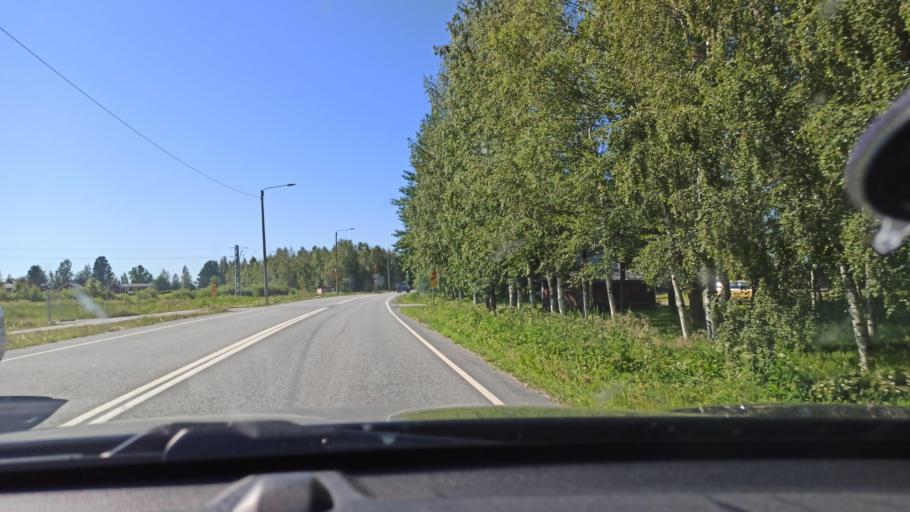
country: FI
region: Ostrobothnia
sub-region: Jakobstadsregionen
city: Bennaes
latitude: 63.6077
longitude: 22.7773
